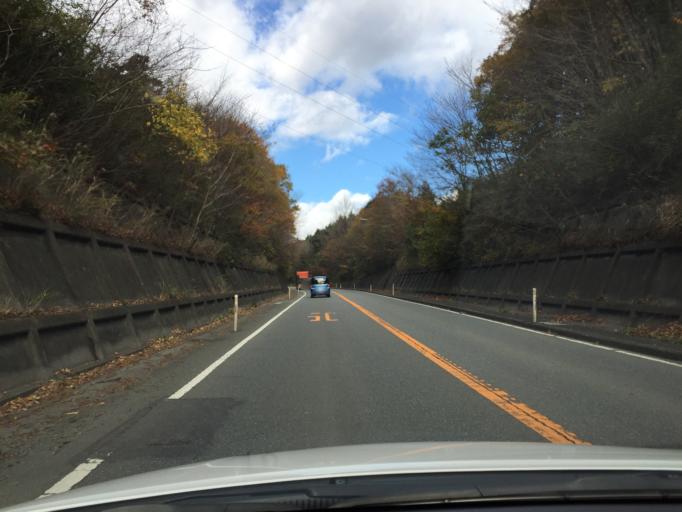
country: JP
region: Fukushima
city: Namie
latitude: 37.3914
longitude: 141.0071
